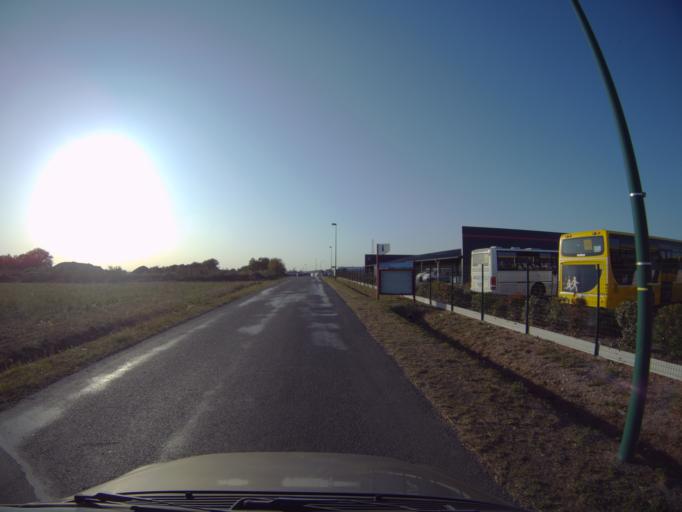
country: FR
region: Pays de la Loire
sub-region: Departement de la Loire-Atlantique
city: Getigne
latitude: 47.0734
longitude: -1.2289
